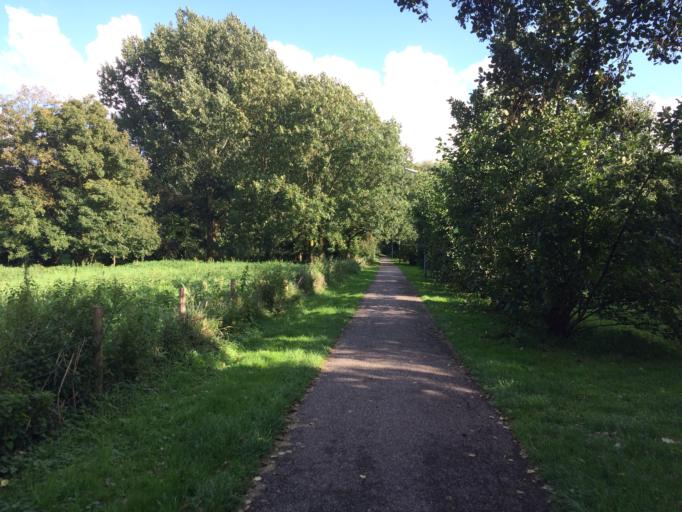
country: NL
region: North Holland
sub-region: Gemeente Uithoorn
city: Uithoorn
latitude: 52.2455
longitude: 4.8362
